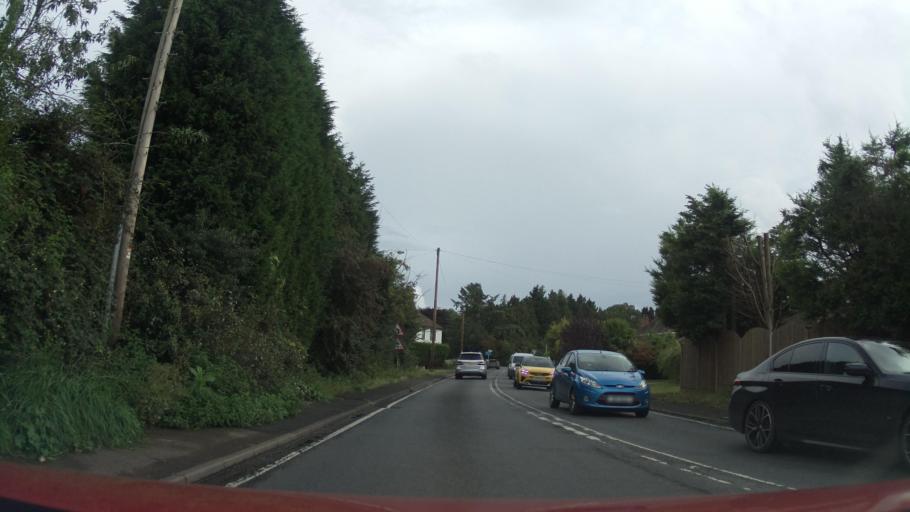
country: GB
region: England
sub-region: Worcestershire
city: Kidderminster
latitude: 52.3656
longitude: -2.1932
